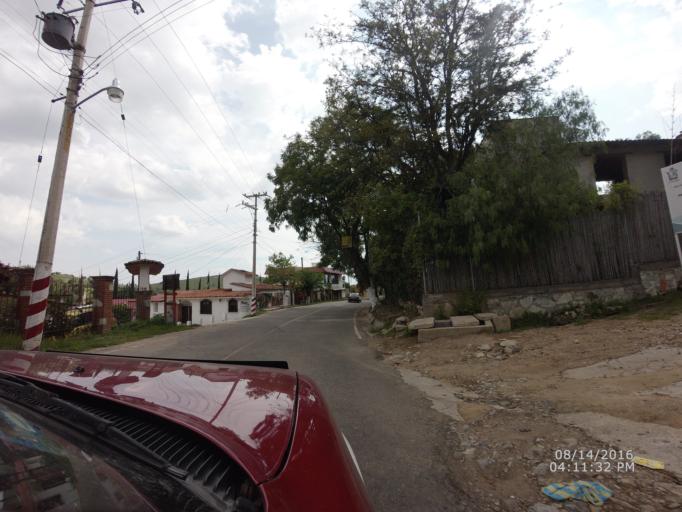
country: MX
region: Oaxaca
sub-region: San Lorenzo Cacaotepec
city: Santiago Etla
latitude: 17.1792
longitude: -96.7672
